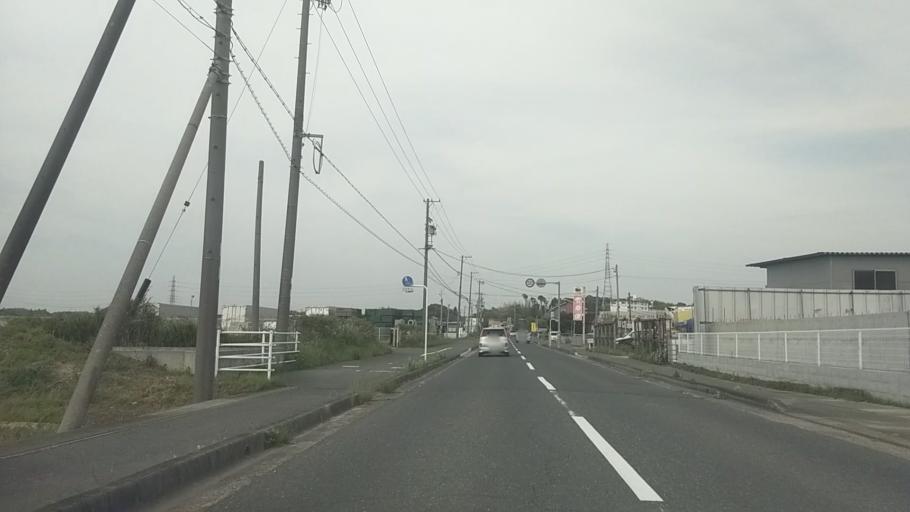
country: JP
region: Shizuoka
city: Hamamatsu
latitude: 34.7389
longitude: 137.6482
